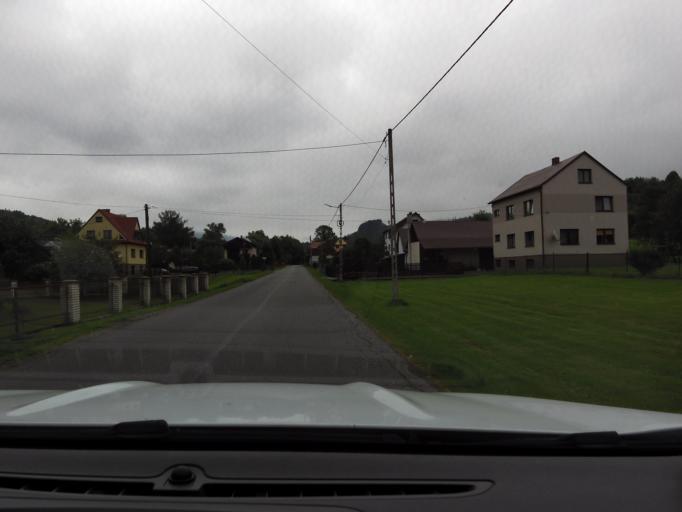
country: PL
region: Silesian Voivodeship
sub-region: Powiat zywiecki
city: Ujsoly
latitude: 49.4793
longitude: 19.1470
